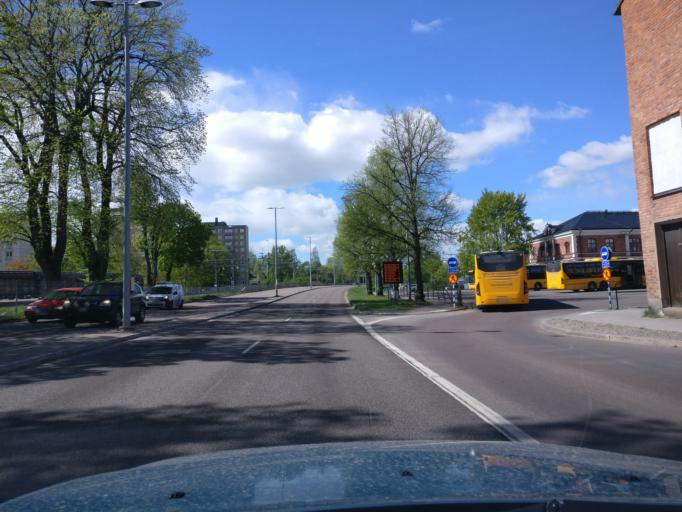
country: SE
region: Vaermland
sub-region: Karlstads Kommun
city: Karlstad
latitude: 59.3784
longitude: 13.4938
